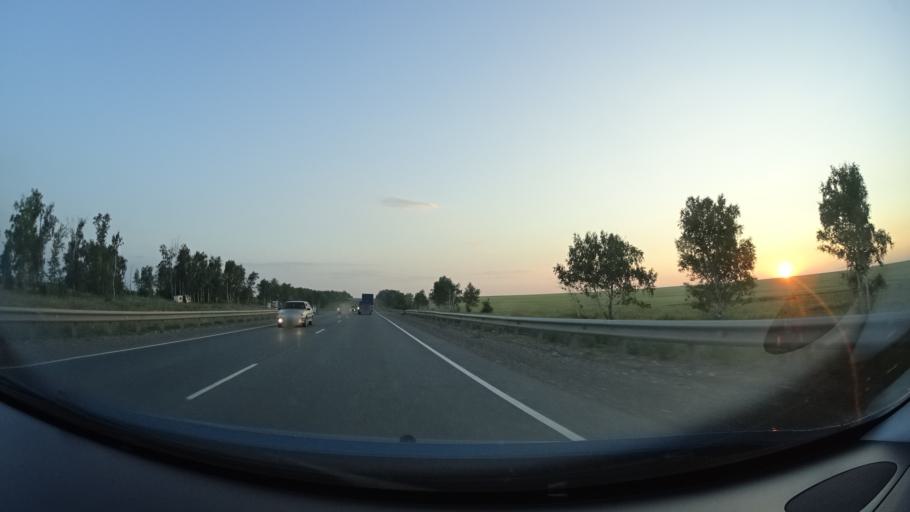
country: RU
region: Samara
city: Sukhodol
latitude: 53.8377
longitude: 51.1017
